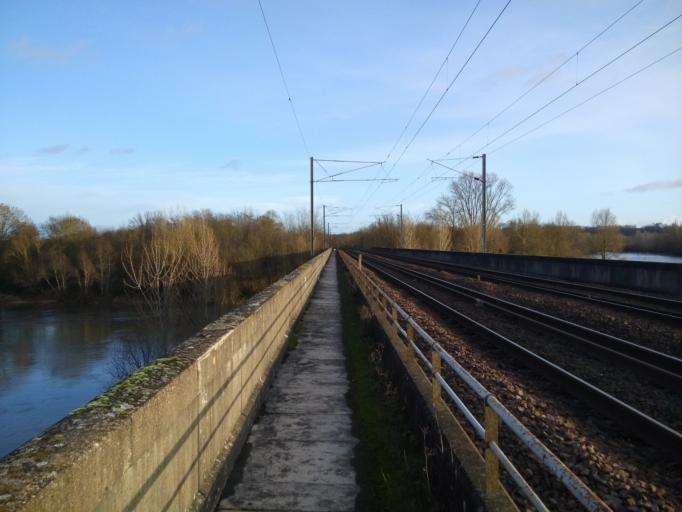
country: FR
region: Centre
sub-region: Departement d'Indre-et-Loire
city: Cinq-Mars-la-Pile
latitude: 47.3445
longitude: 0.4794
